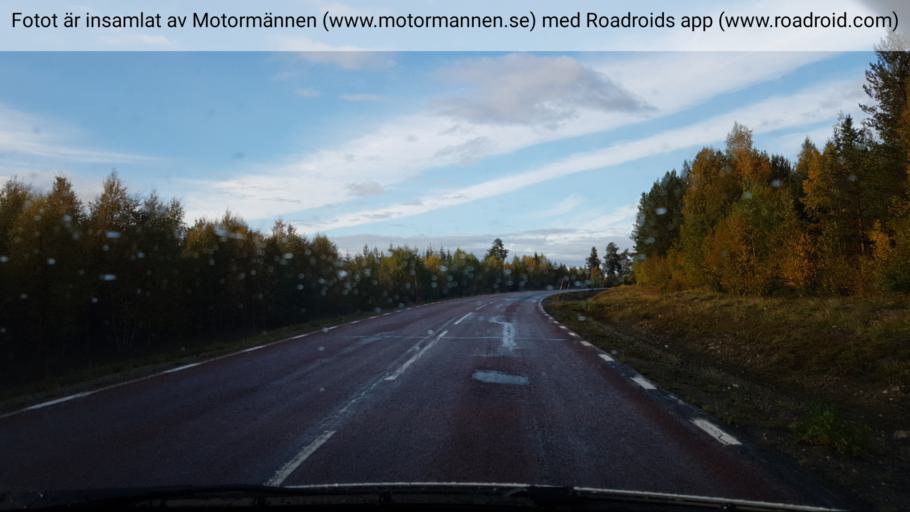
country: SE
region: Vaesterbotten
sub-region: Dorotea Kommun
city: Dorotea
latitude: 64.1392
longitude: 16.2231
